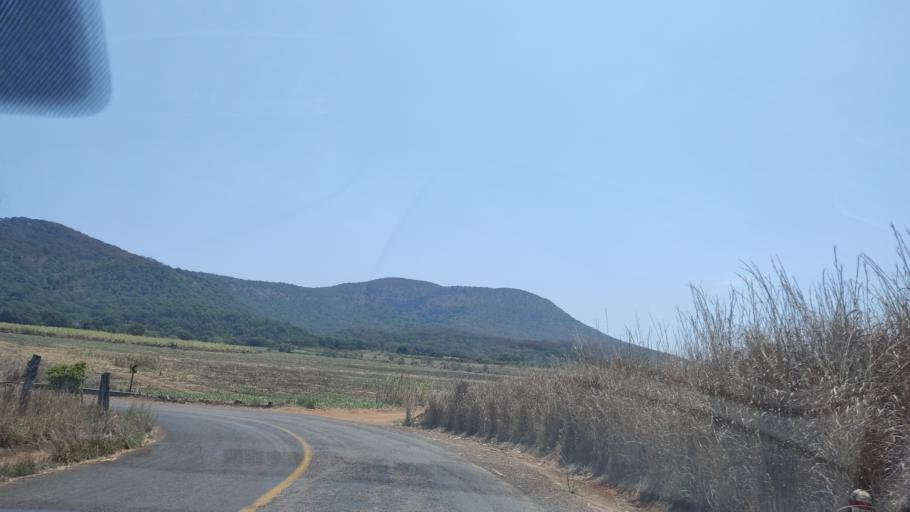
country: MX
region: Nayarit
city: Puga
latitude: 21.5737
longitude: -104.7565
